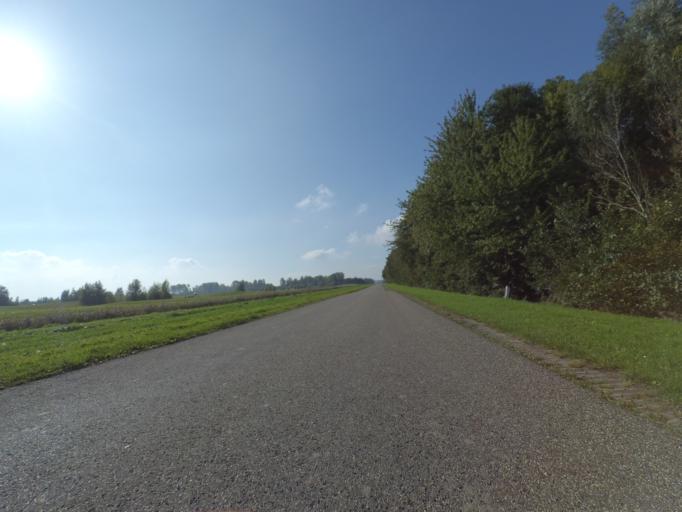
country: NL
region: Flevoland
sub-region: Gemeente Dronten
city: Biddinghuizen
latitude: 52.4109
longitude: 5.6820
